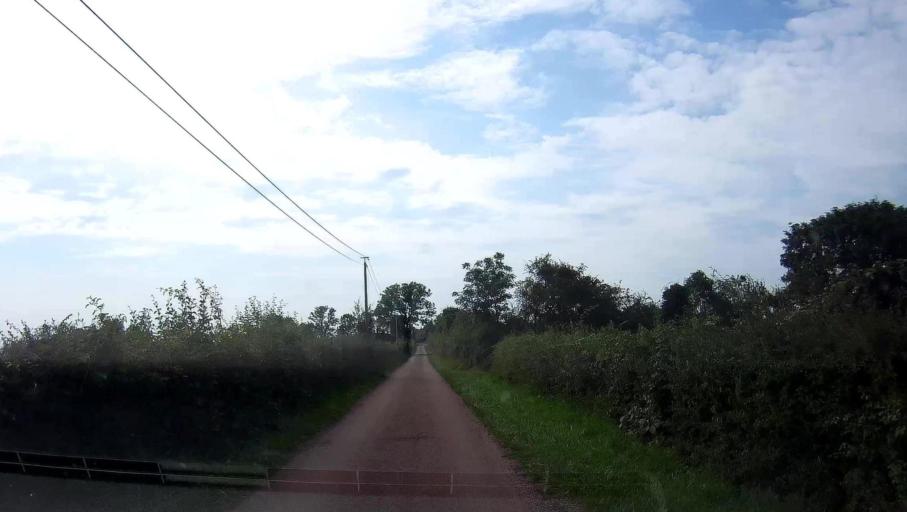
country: FR
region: Bourgogne
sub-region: Departement de Saone-et-Loire
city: Saint-Leger-sur-Dheune
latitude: 46.8953
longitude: 4.6147
